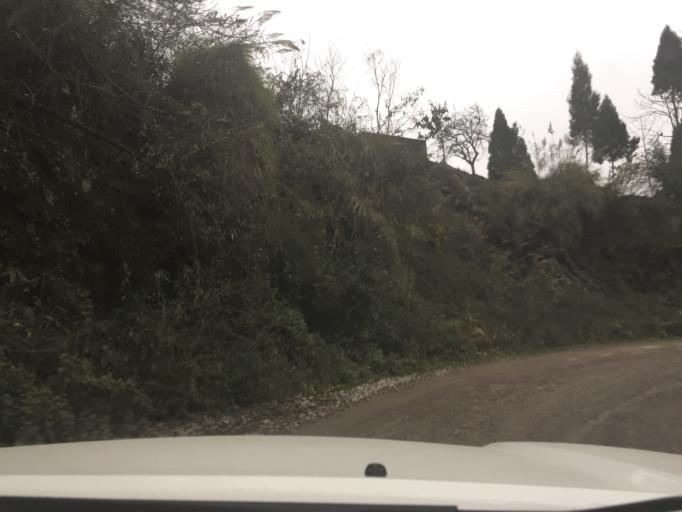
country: CN
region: Guizhou Sheng
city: Zunyi
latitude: 27.2164
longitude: 106.8737
